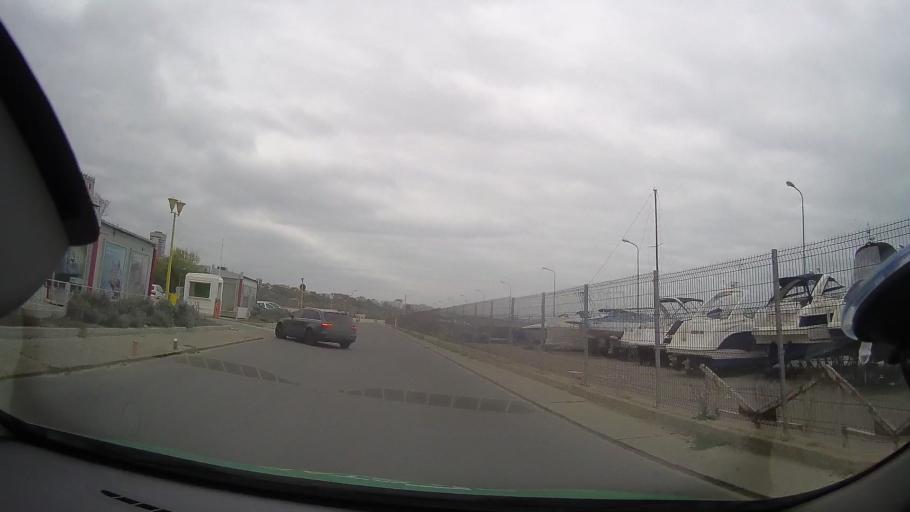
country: RO
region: Constanta
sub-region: Municipiul Constanta
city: Constanta
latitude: 44.1765
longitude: 28.6599
